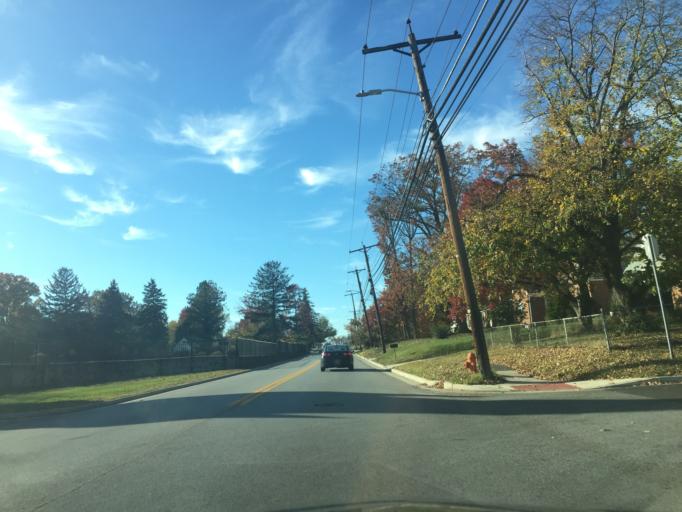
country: US
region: Maryland
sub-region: Baltimore County
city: Parkville
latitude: 39.3819
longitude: -76.5624
